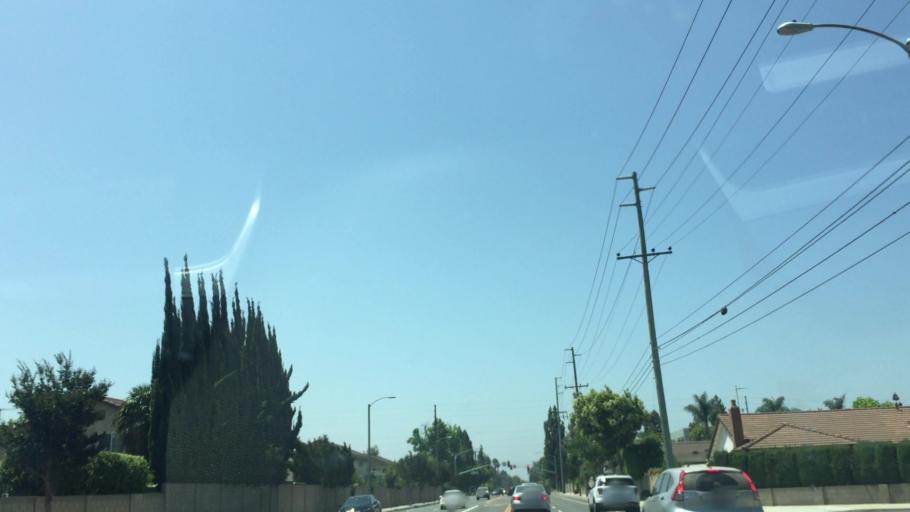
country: US
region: California
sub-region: Orange County
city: Fountain Valley
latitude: 33.7185
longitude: -117.9285
